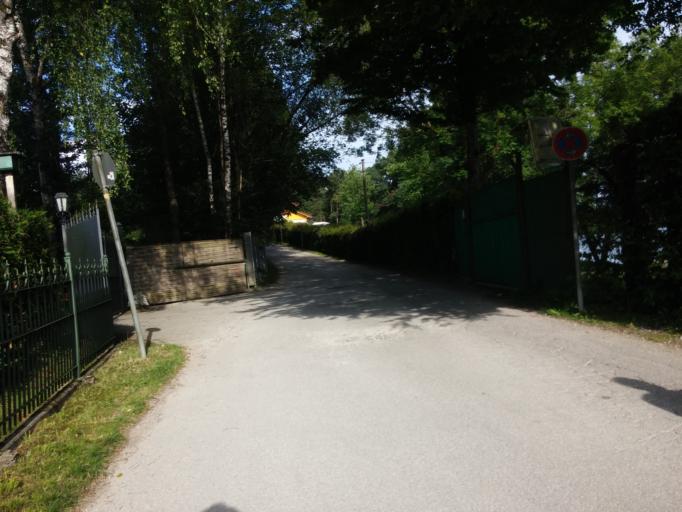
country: DE
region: Bavaria
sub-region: Upper Bavaria
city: Moosach
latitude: 48.0243
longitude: 11.8577
